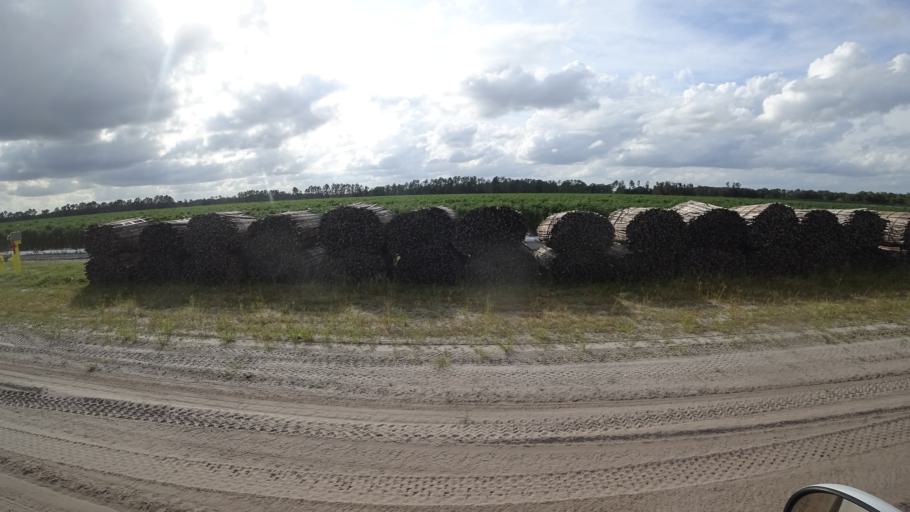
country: US
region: Florida
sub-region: Hillsborough County
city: Balm
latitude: 27.6226
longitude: -82.1338
